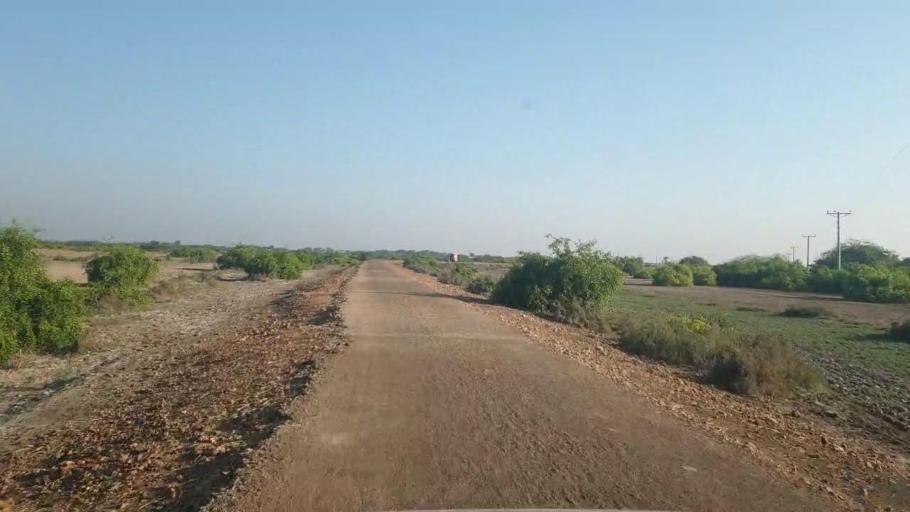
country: PK
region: Sindh
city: Badin
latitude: 24.7339
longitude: 68.8688
